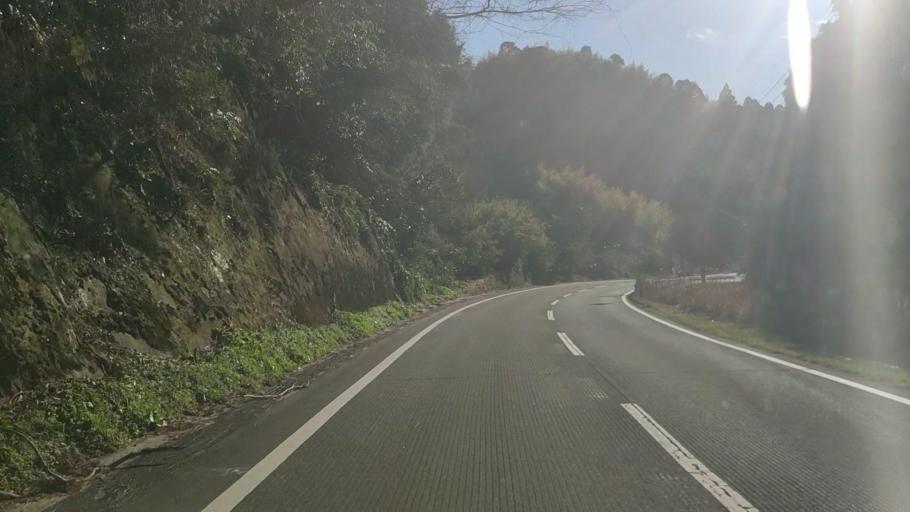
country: JP
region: Saga Prefecture
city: Kanzakimachi-kanzaki
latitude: 33.3940
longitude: 130.2710
